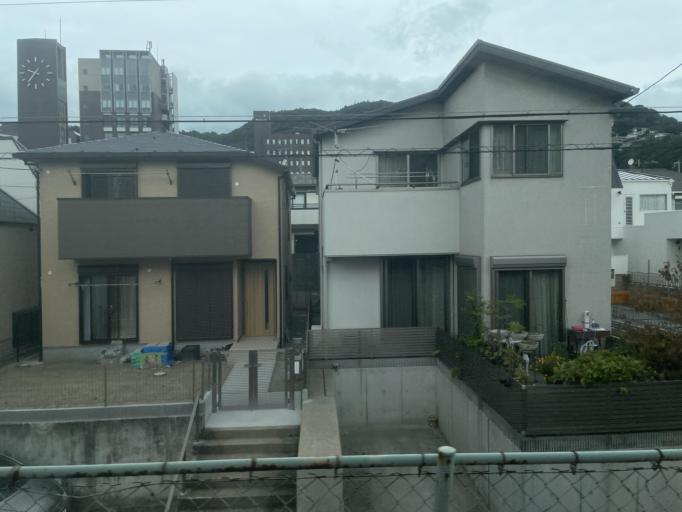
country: JP
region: Hyogo
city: Ashiya
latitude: 34.7278
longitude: 135.2694
